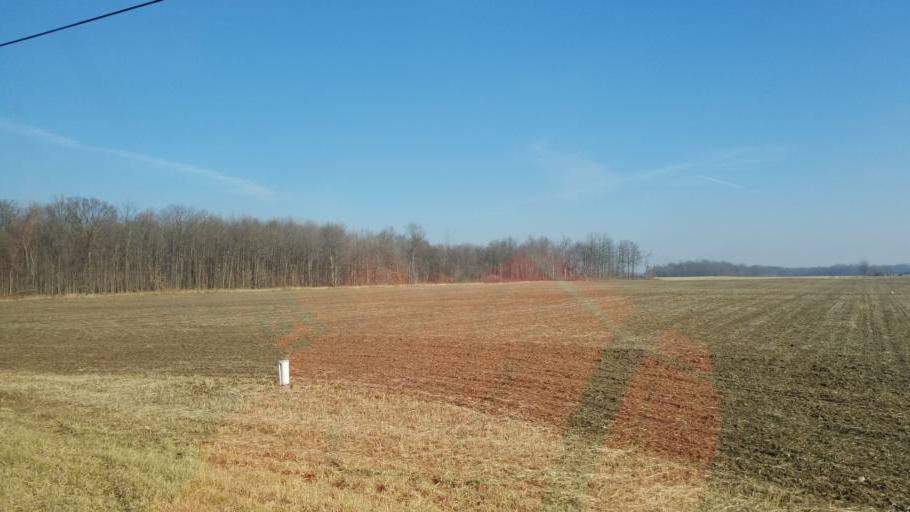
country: US
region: Ohio
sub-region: Crawford County
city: Bucyrus
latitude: 40.8678
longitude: -82.9879
